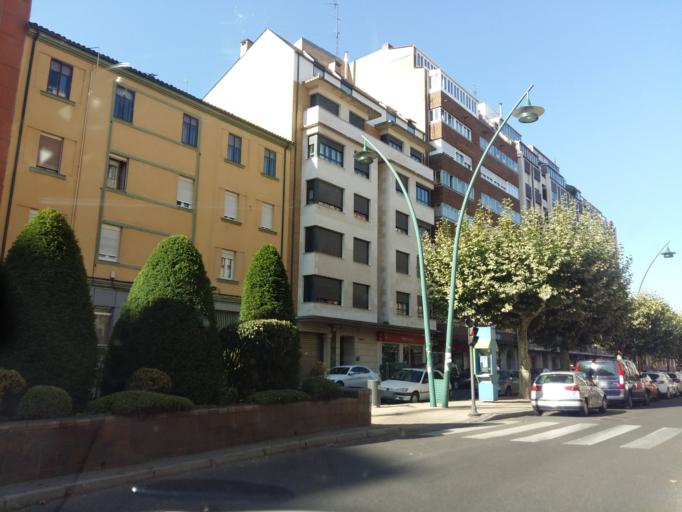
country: ES
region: Castille and Leon
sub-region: Provincia de Leon
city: Leon
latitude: 42.5940
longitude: -5.5738
